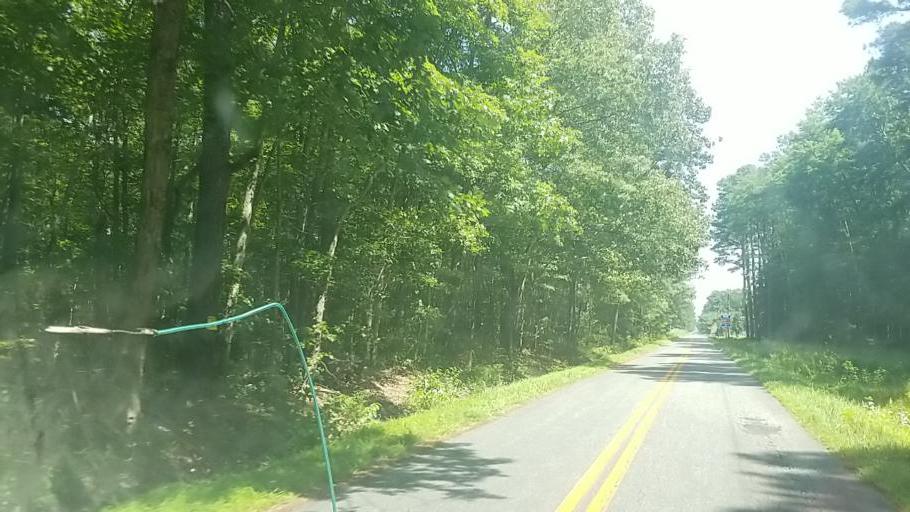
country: US
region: Maryland
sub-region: Wicomico County
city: Hebron
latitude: 38.4227
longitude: -75.8716
